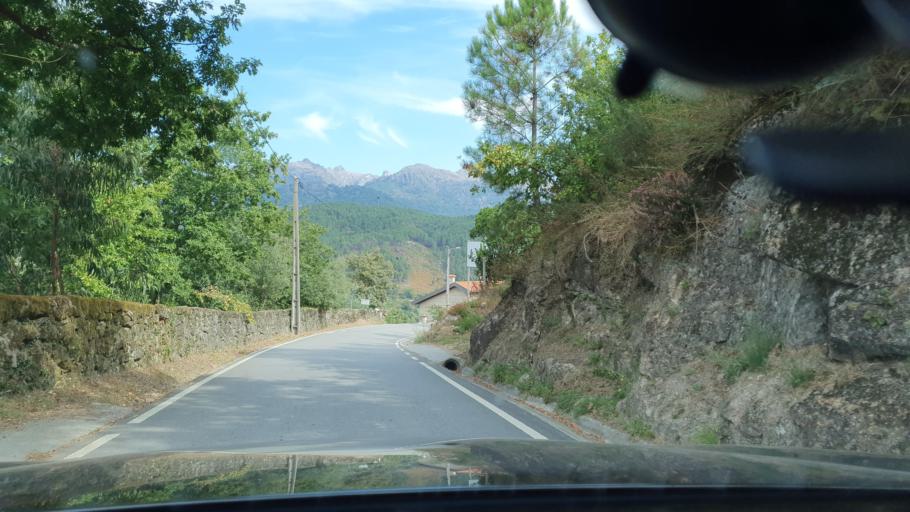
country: PT
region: Braga
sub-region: Vieira do Minho
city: Vieira do Minho
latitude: 41.6856
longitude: -8.0989
